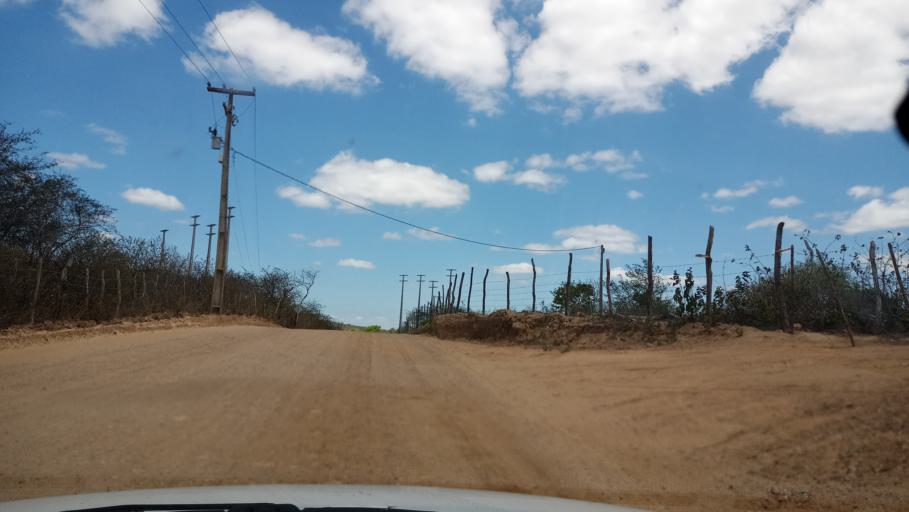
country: BR
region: Rio Grande do Norte
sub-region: Sao Paulo Do Potengi
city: Sao Paulo do Potengi
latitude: -5.7894
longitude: -35.9172
